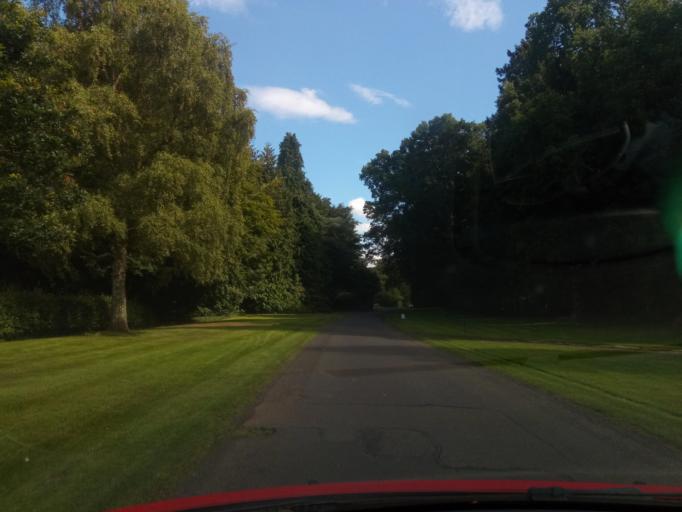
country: GB
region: Scotland
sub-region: The Scottish Borders
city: Coldstream
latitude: 55.6496
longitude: -2.2631
